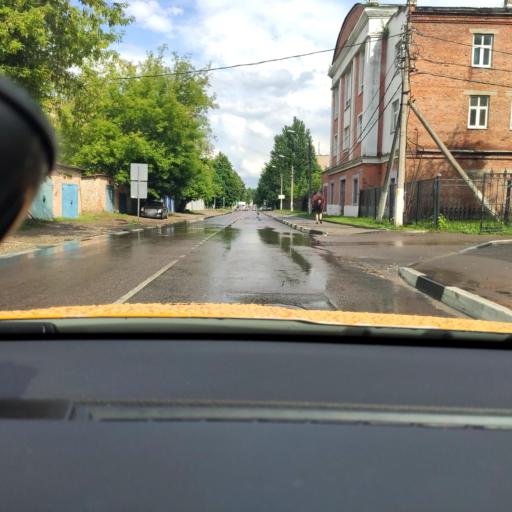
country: RU
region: Moskovskaya
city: Stupino
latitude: 54.8902
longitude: 38.0698
